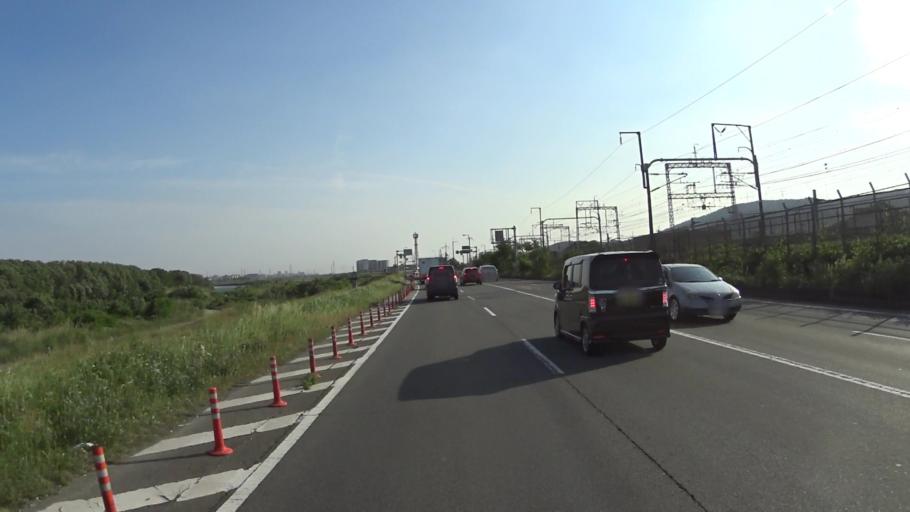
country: JP
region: Kyoto
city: Yawata
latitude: 34.8903
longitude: 135.6800
